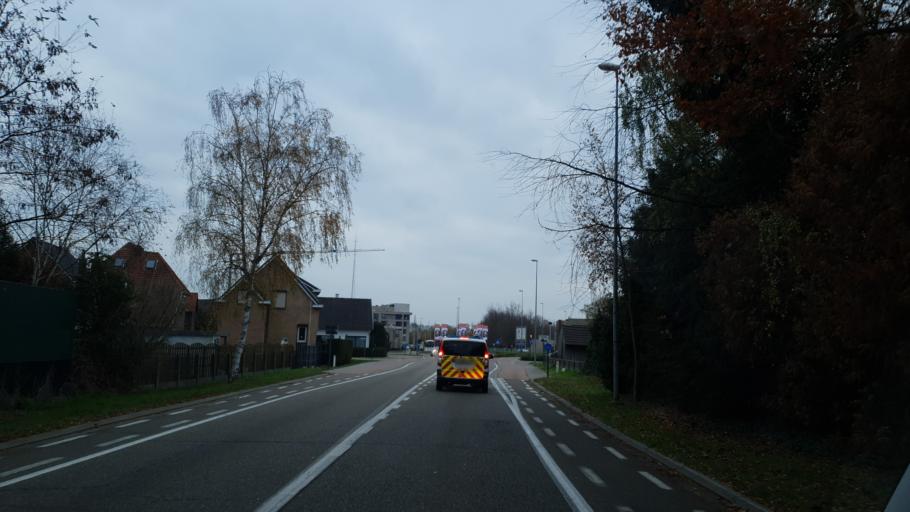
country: BE
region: Flanders
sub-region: Provincie Limburg
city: Lanaken
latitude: 50.8928
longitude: 5.6556
